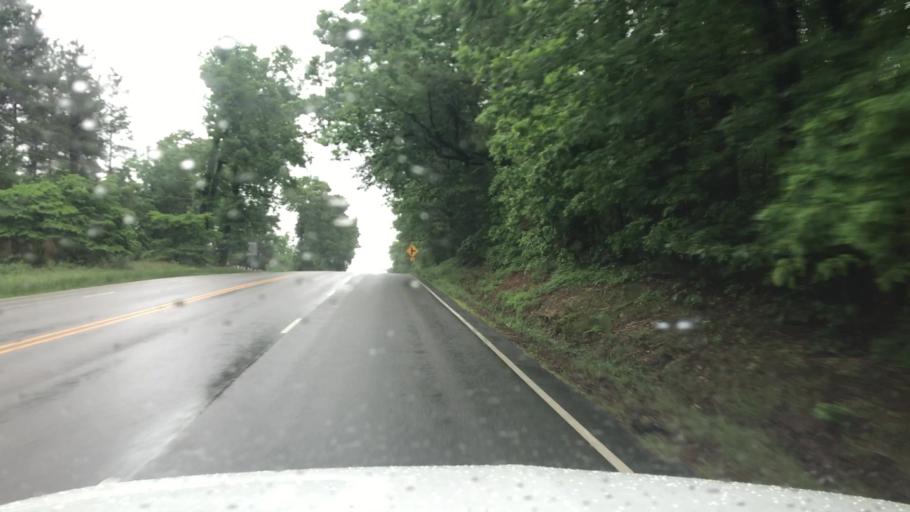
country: US
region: Virginia
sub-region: Hanover County
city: Ashland
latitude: 37.8414
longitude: -77.4661
